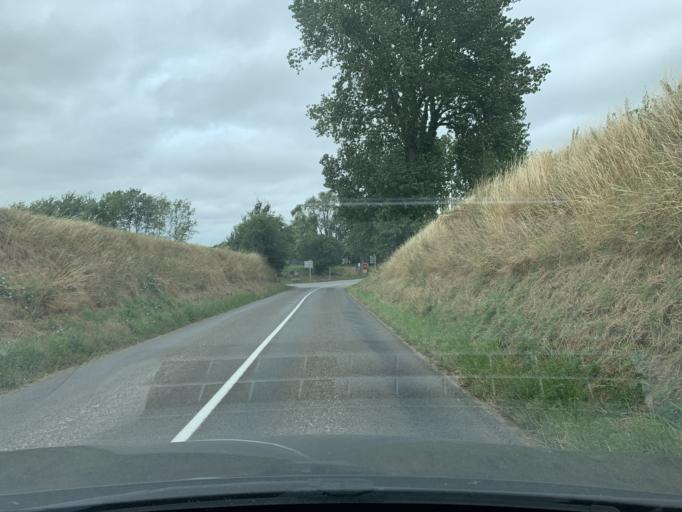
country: FR
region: Nord-Pas-de-Calais
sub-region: Departement du Nord
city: Fechain
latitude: 50.2330
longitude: 3.2174
